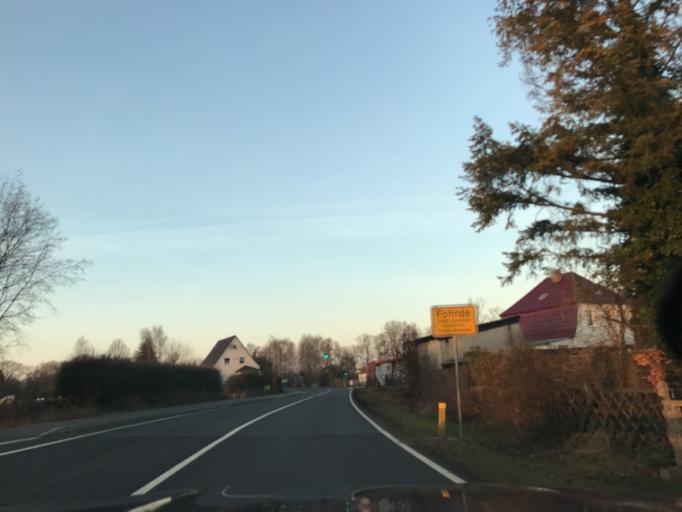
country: DE
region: Brandenburg
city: Brandenburg an der Havel
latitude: 52.4882
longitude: 12.4624
